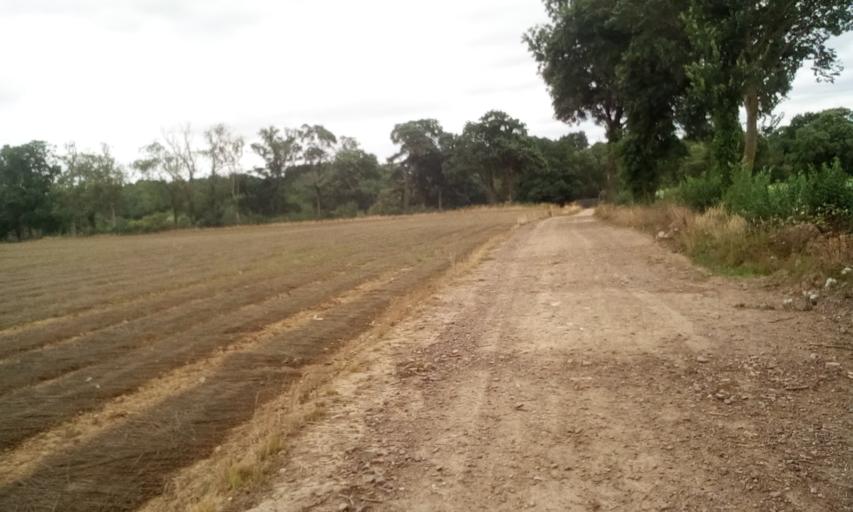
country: FR
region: Lower Normandy
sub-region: Departement du Calvados
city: Tourville-sur-Odon
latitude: 49.1366
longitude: -0.4950
